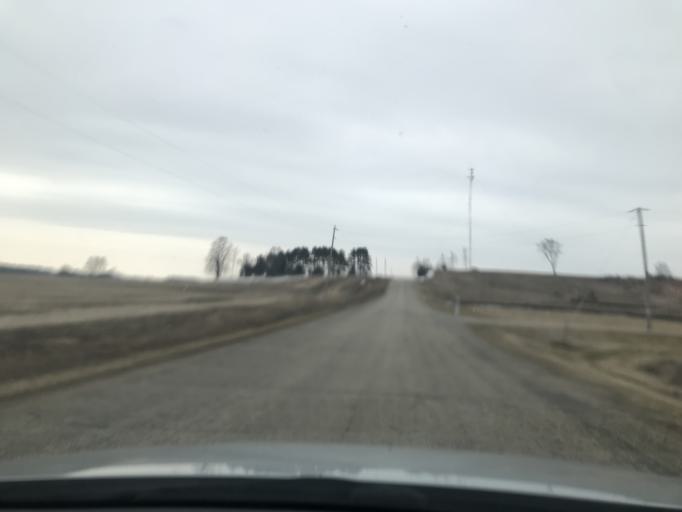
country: US
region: Wisconsin
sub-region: Marinette County
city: Peshtigo
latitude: 45.0993
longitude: -87.9324
